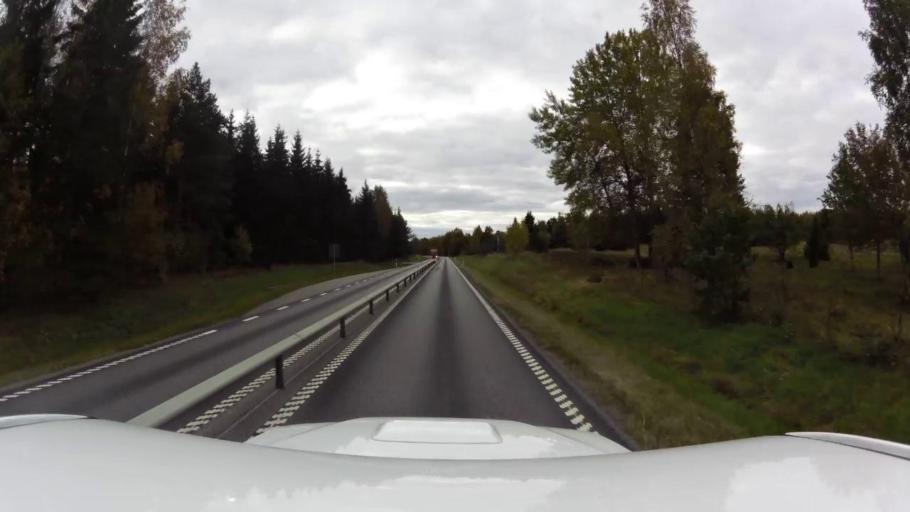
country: SE
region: OEstergoetland
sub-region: Linkopings Kommun
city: Malmslatt
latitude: 58.2963
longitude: 15.5642
